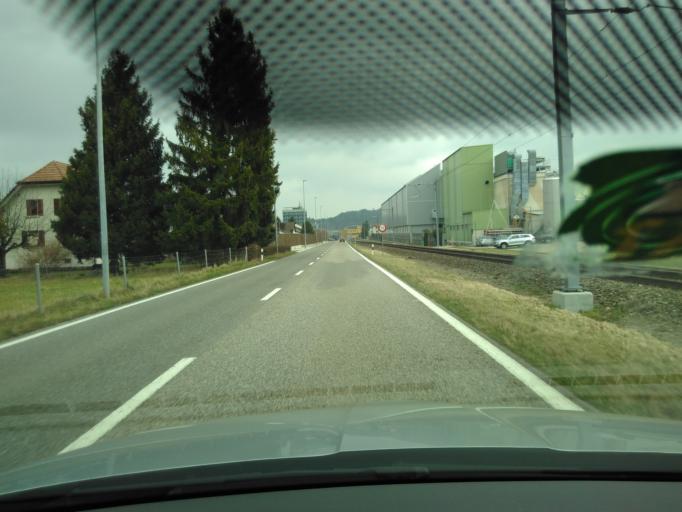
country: CH
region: Aargau
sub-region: Bezirk Aarau
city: Suhr
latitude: 47.3664
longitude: 8.0735
